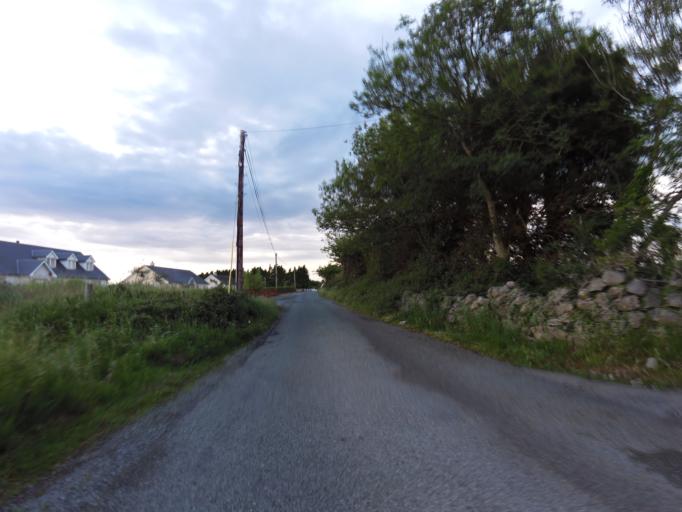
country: IE
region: Connaught
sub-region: County Galway
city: Athenry
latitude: 53.2953
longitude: -8.7324
